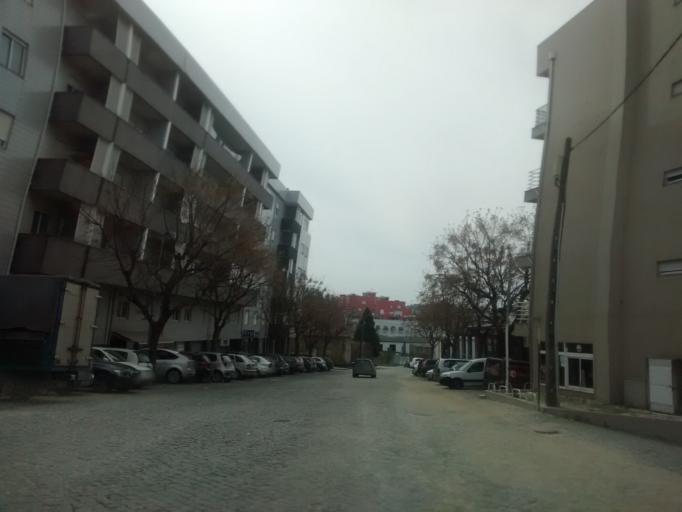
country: PT
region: Braga
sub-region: Braga
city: Braga
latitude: 41.5571
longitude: -8.4036
